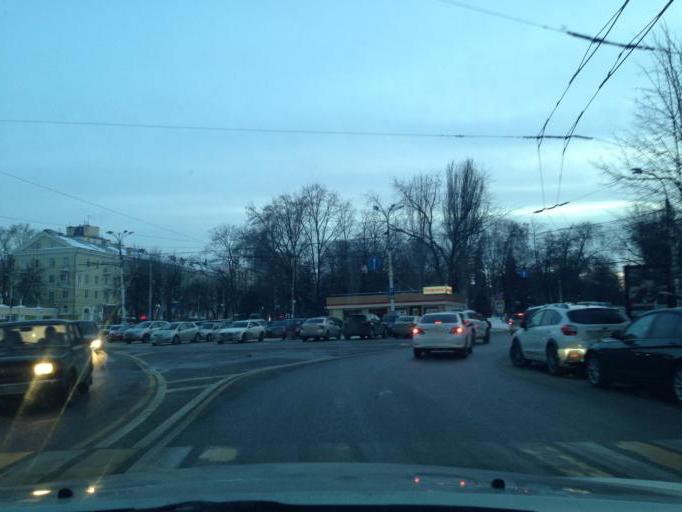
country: RU
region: Voronezj
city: Voronezh
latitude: 51.6633
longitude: 39.2038
